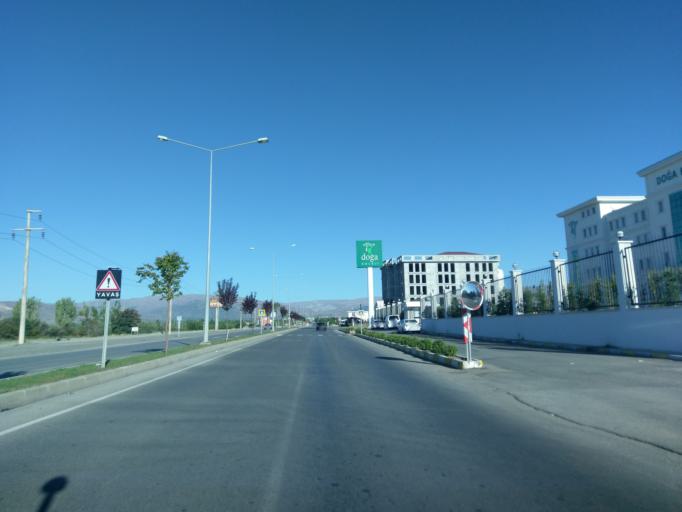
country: TR
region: Erzincan
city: Erzincan
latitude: 39.7643
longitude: 39.4361
